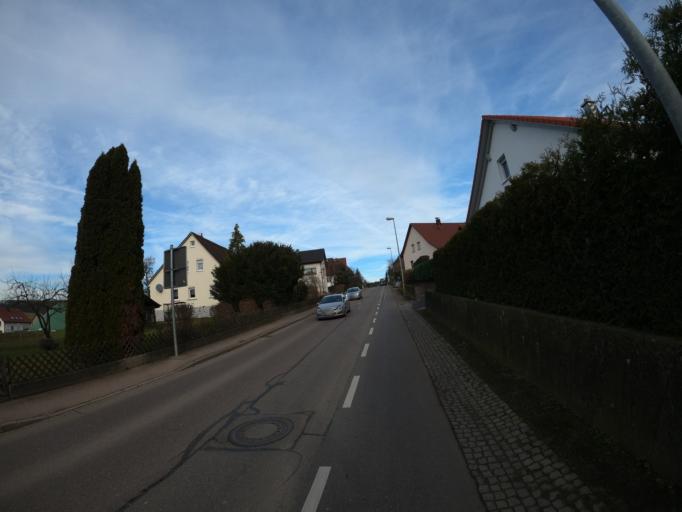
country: DE
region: Baden-Wuerttemberg
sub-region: Regierungsbezirk Stuttgart
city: Salach
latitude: 48.7075
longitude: 9.7348
